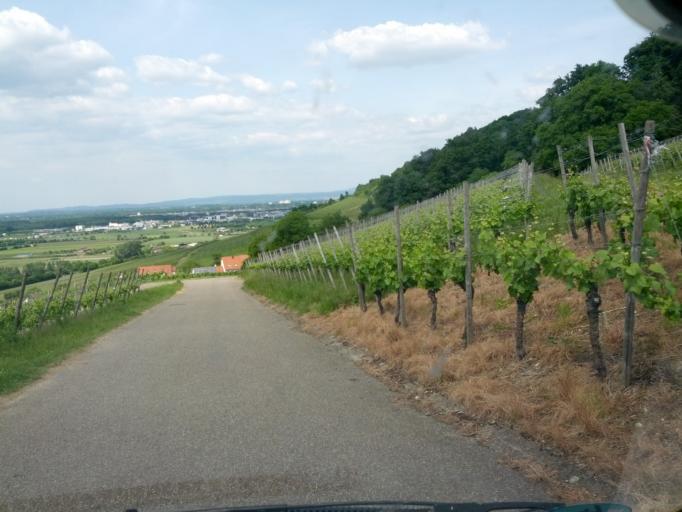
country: DE
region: Baden-Wuerttemberg
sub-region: Freiburg Region
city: Ebringen
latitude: 47.9634
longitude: 7.7815
